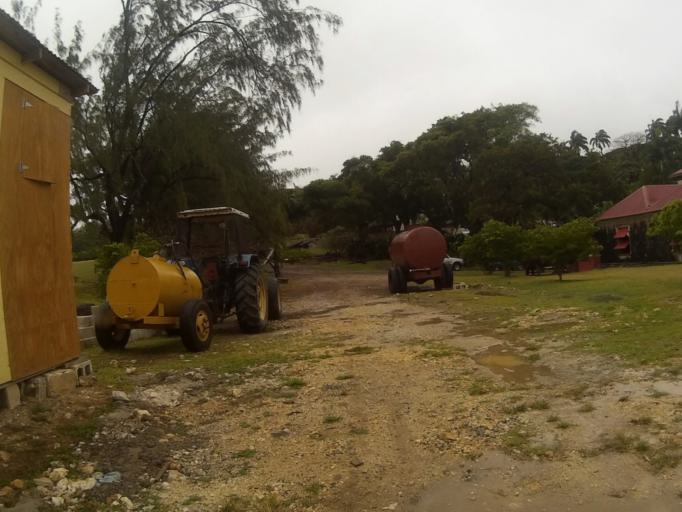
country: BB
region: Saint Andrew
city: Greenland
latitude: 13.2780
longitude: -59.5894
